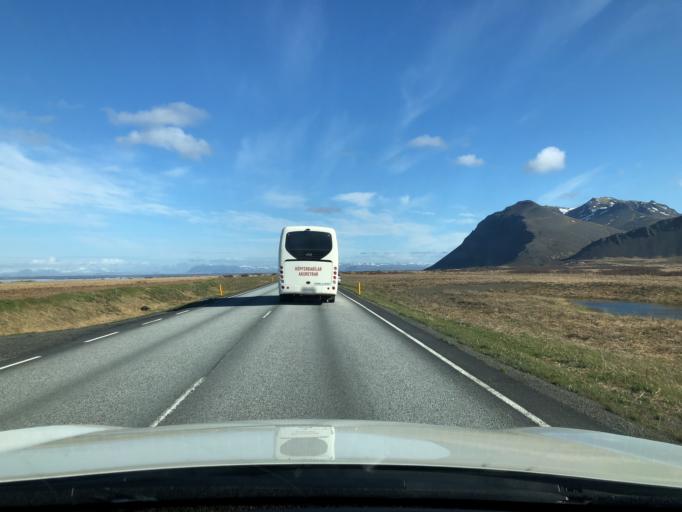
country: IS
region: West
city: Borgarnes
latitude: 64.4381
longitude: -21.9579
